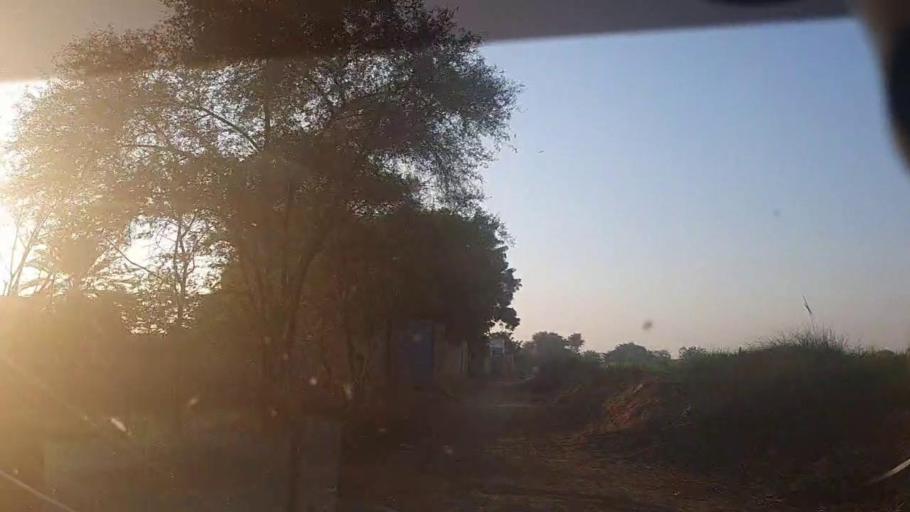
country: PK
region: Sindh
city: Sobhadero
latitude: 27.3626
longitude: 68.4129
